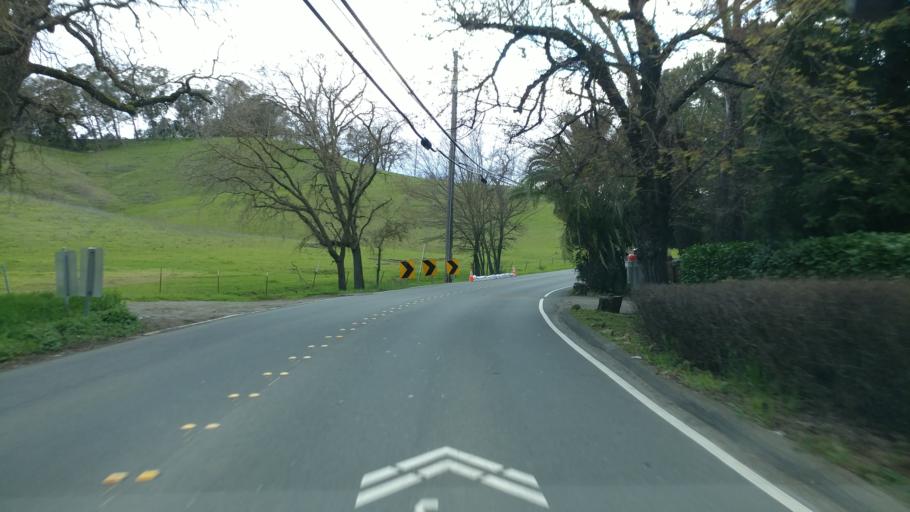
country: US
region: California
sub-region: Contra Costa County
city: Diablo
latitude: 37.8319
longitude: -121.9563
